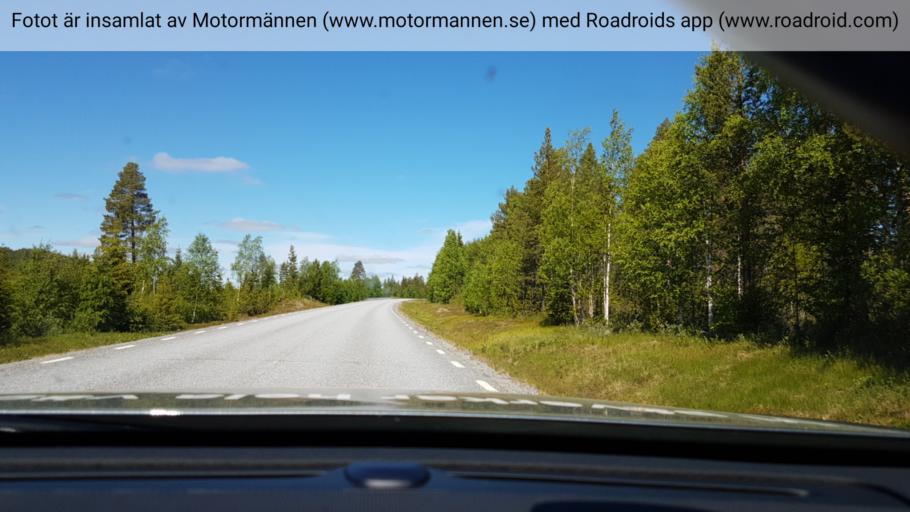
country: SE
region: Vaesterbotten
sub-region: Vilhelmina Kommun
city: Vilhelmina
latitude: 64.4076
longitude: 16.8235
